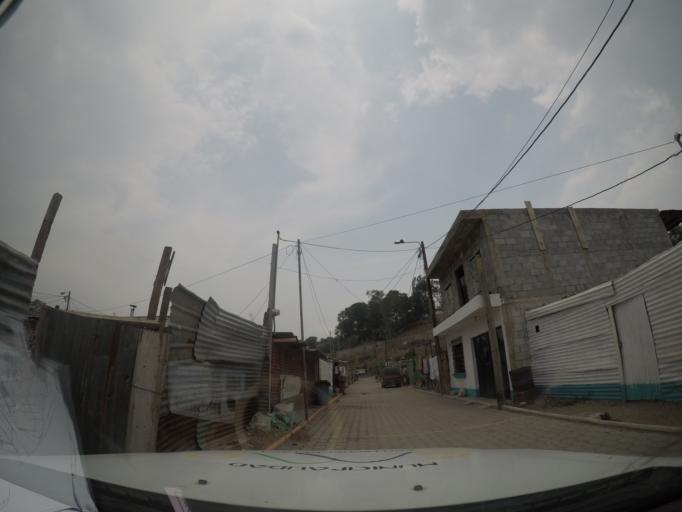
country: GT
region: Guatemala
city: Petapa
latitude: 14.5051
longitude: -90.5484
